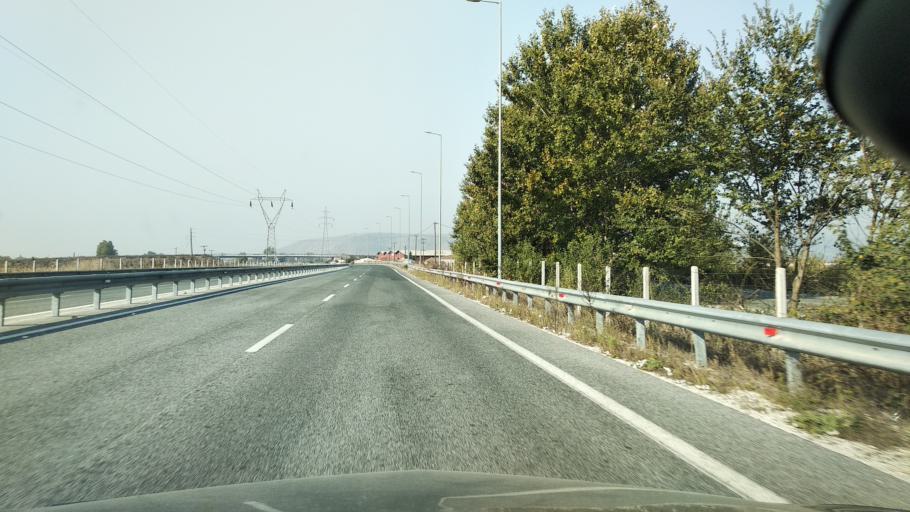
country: GR
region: Thessaly
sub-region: Trikala
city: Oichalia
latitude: 39.5794
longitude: 22.0181
